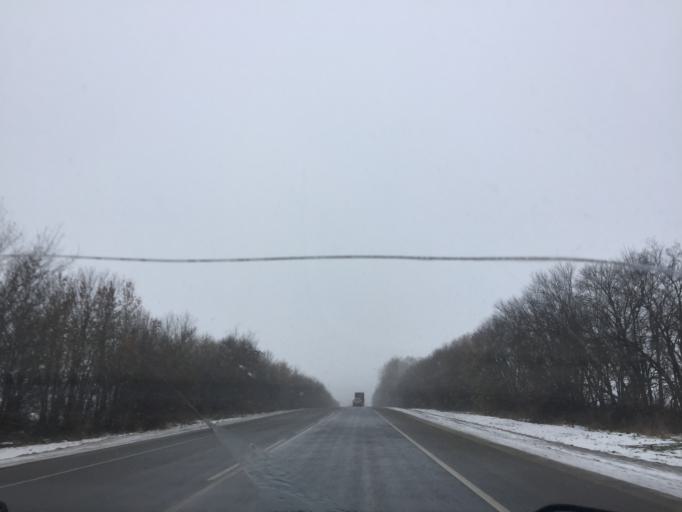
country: RU
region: Tula
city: Plavsk
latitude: 53.7922
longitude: 37.3710
